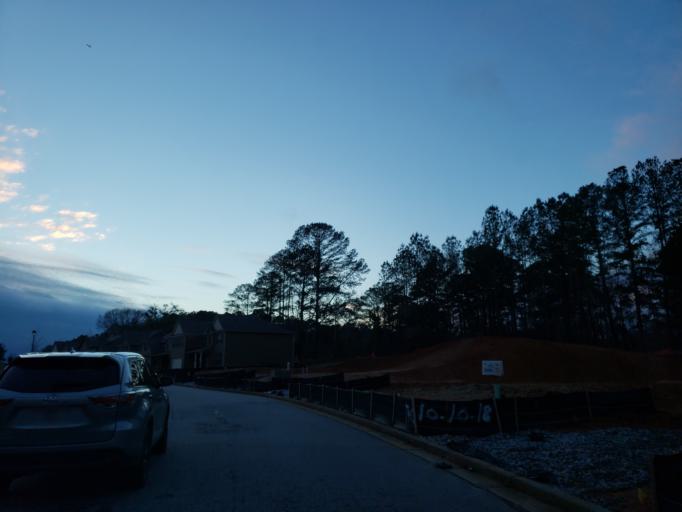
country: US
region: Georgia
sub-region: Fulton County
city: Union City
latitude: 33.6924
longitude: -84.5895
